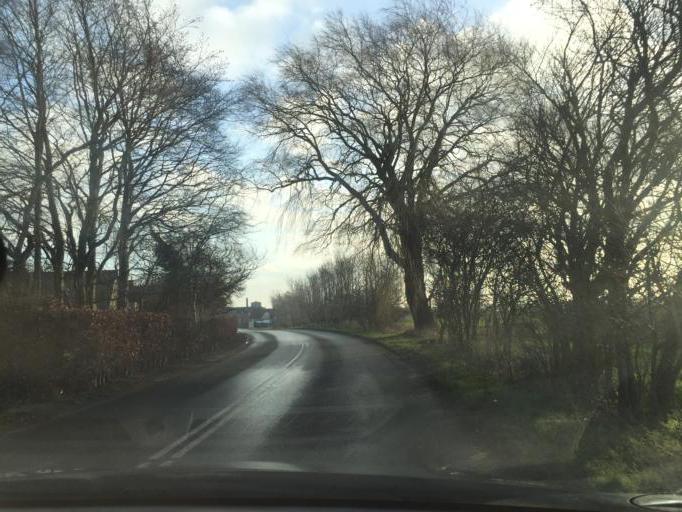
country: DK
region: South Denmark
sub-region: Faaborg-Midtfyn Kommune
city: Ringe
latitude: 55.1951
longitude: 10.3441
